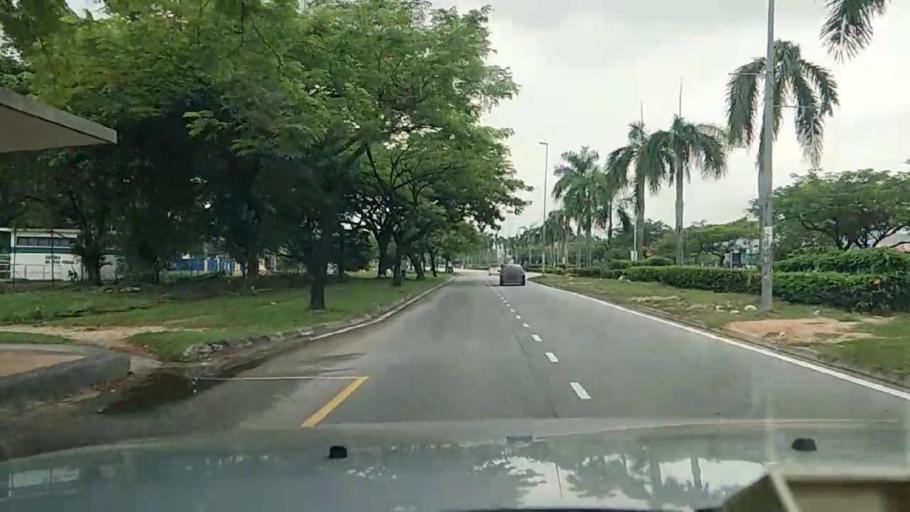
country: MY
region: Putrajaya
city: Putrajaya
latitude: 2.9468
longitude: 101.6170
